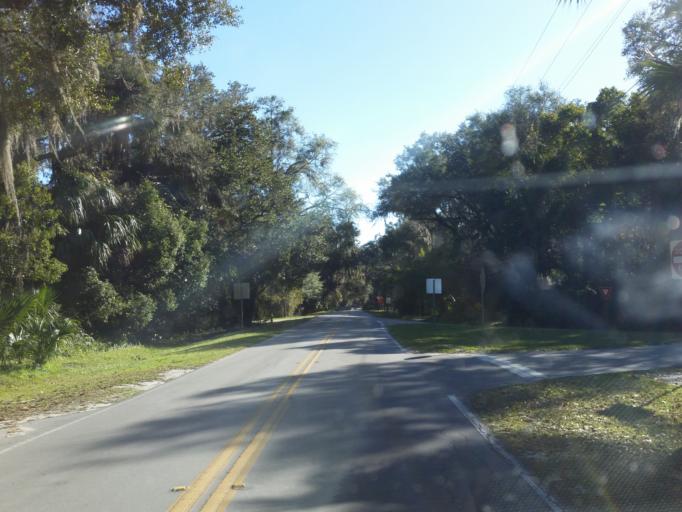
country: US
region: Florida
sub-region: Alachua County
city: Gainesville
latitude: 29.5106
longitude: -82.2795
